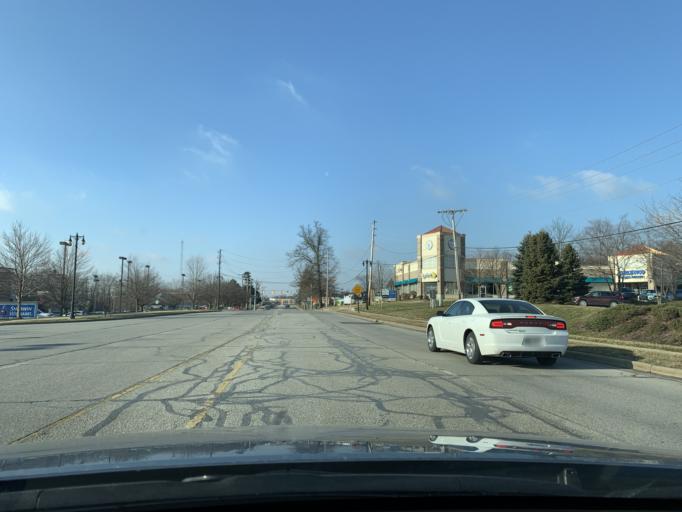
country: US
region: Indiana
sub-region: Porter County
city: Valparaiso
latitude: 41.4683
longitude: -87.0312
